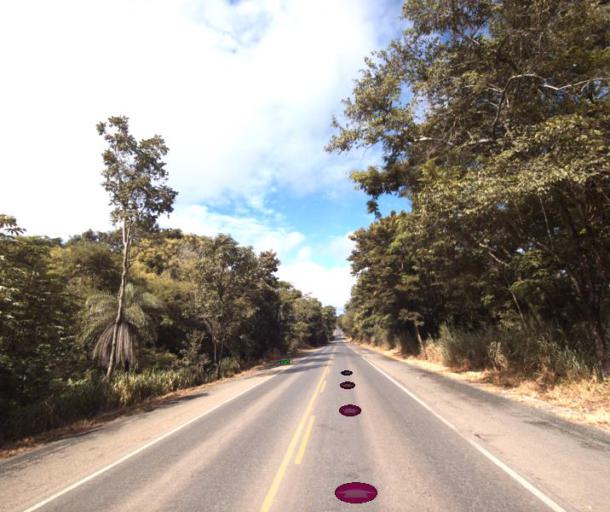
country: BR
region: Goias
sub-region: Uruacu
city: Uruacu
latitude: -14.7331
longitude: -49.2400
